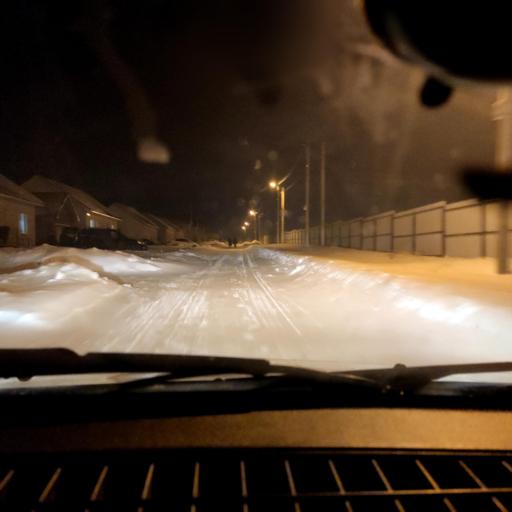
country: RU
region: Bashkortostan
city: Mikhaylovka
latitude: 54.7854
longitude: 55.8025
